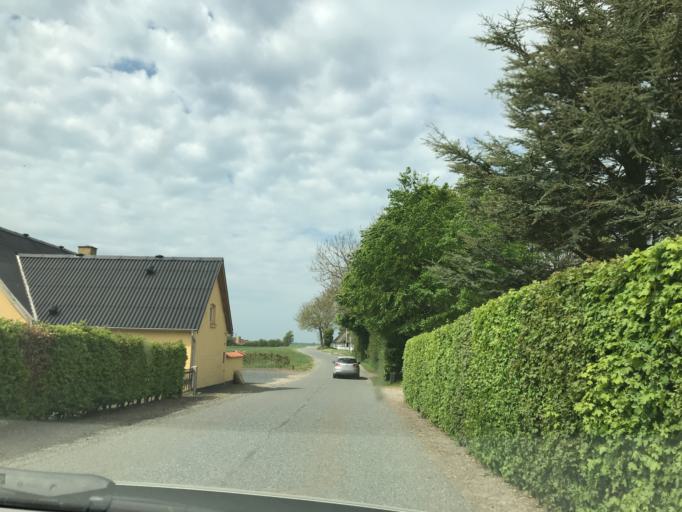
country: DK
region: South Denmark
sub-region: Assens Kommune
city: Assens
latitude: 55.3290
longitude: 9.9008
